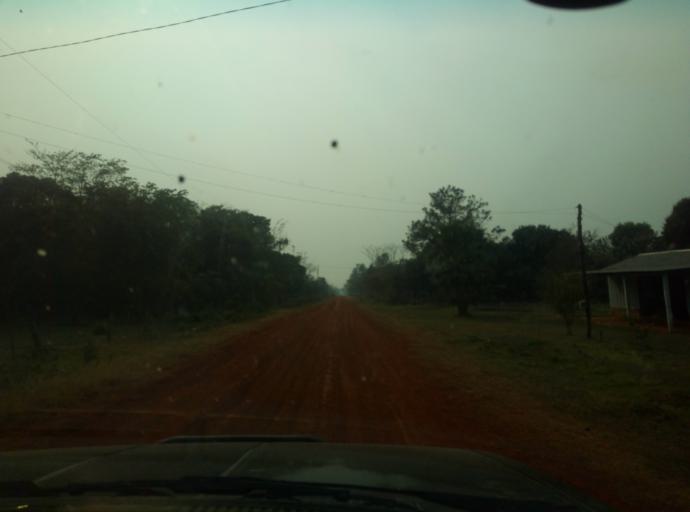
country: PY
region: Caaguazu
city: Carayao
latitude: -25.2042
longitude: -56.2478
